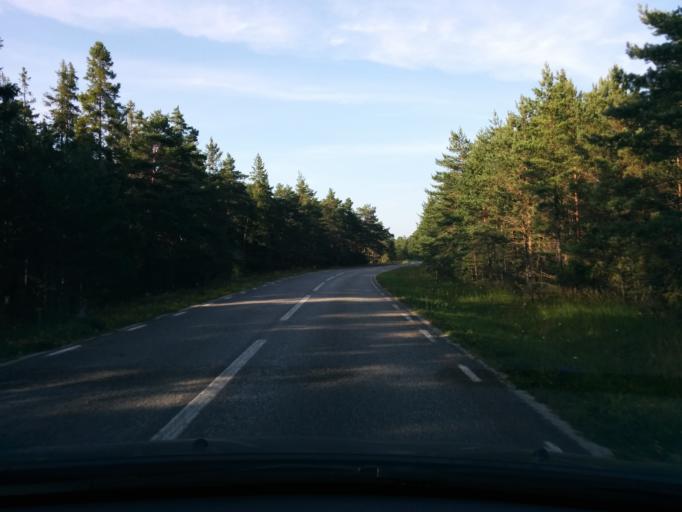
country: SE
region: Gotland
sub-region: Gotland
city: Slite
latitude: 57.5520
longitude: 18.7003
